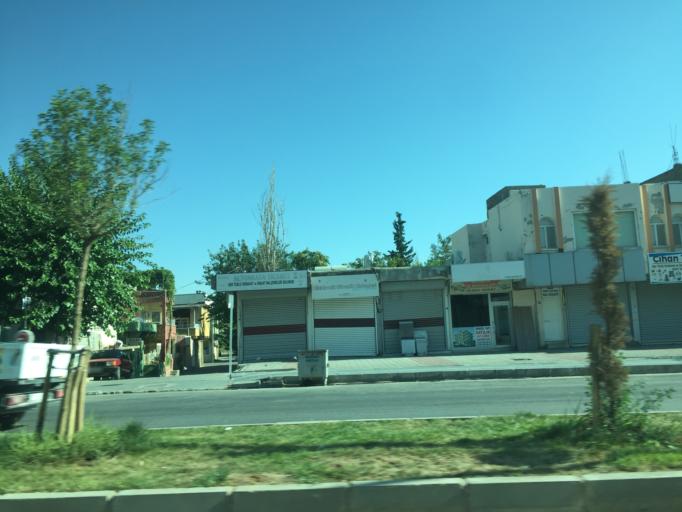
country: TR
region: Mardin
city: Midyat
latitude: 37.4156
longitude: 41.3708
